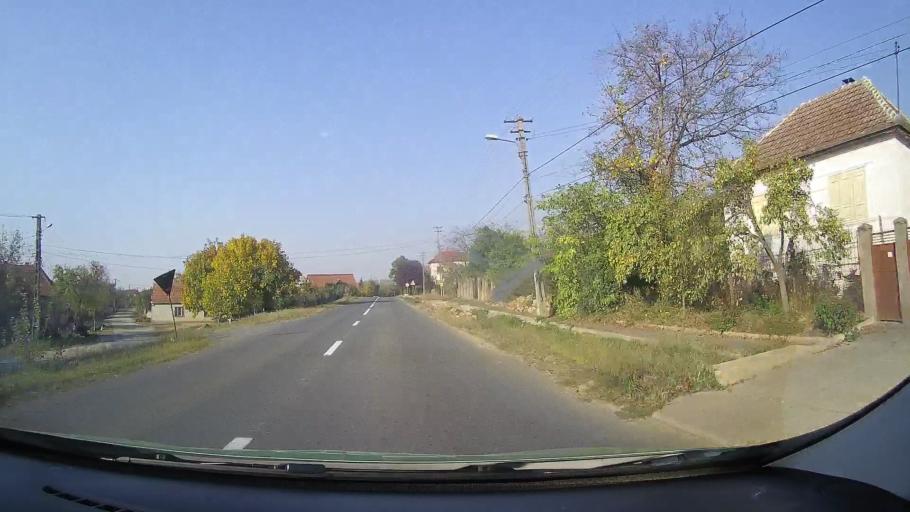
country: RO
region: Arad
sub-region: Comuna Paulis
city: Paulis
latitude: 46.1178
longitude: 21.5965
